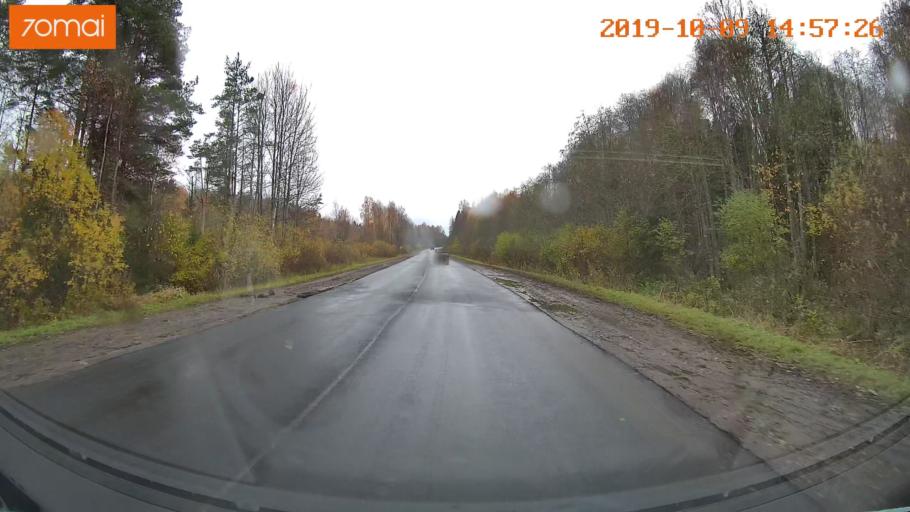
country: RU
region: Kostroma
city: Chistyye Bory
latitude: 58.3377
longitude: 41.6507
